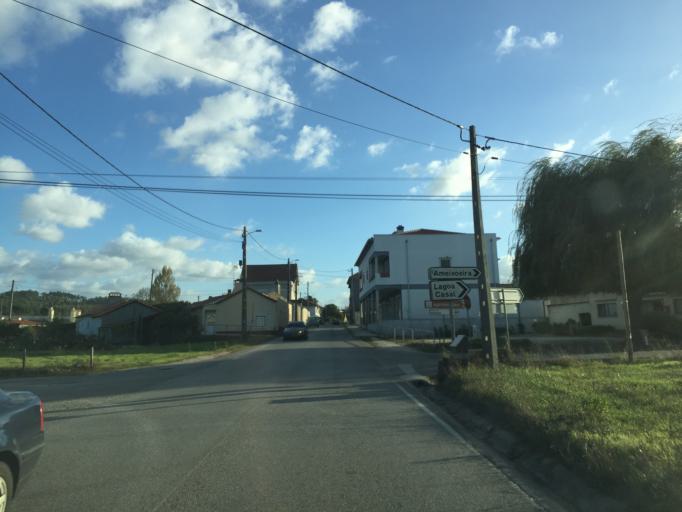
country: PT
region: Leiria
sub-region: Leiria
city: Souto da Carpalhosa
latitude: 39.8322
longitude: -8.8399
